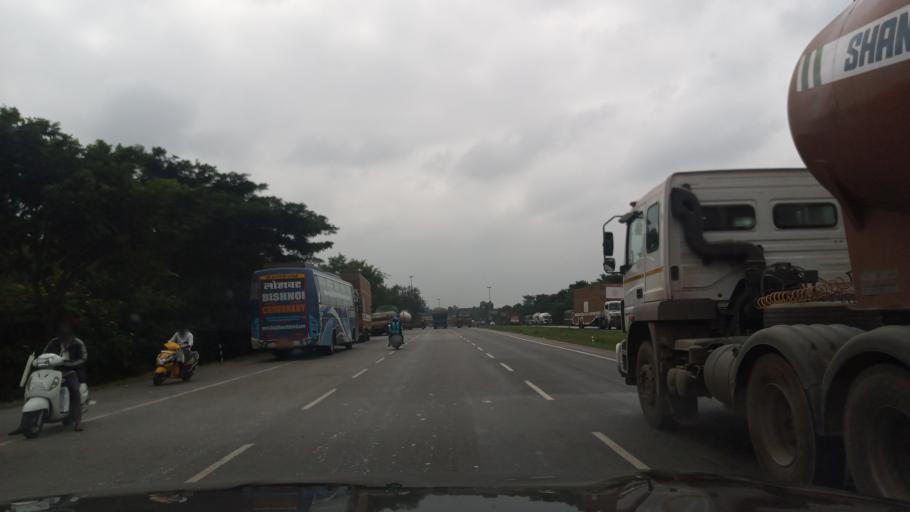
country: IN
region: Karnataka
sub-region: Bangalore Rural
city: Nelamangala
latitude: 13.0487
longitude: 77.4760
